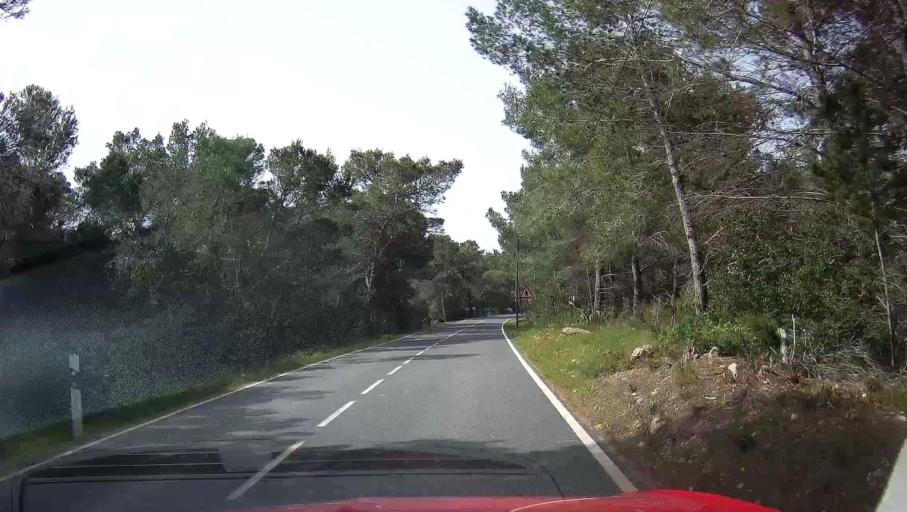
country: ES
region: Balearic Islands
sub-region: Illes Balears
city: Sant Joan de Labritja
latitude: 39.0573
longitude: 1.5822
